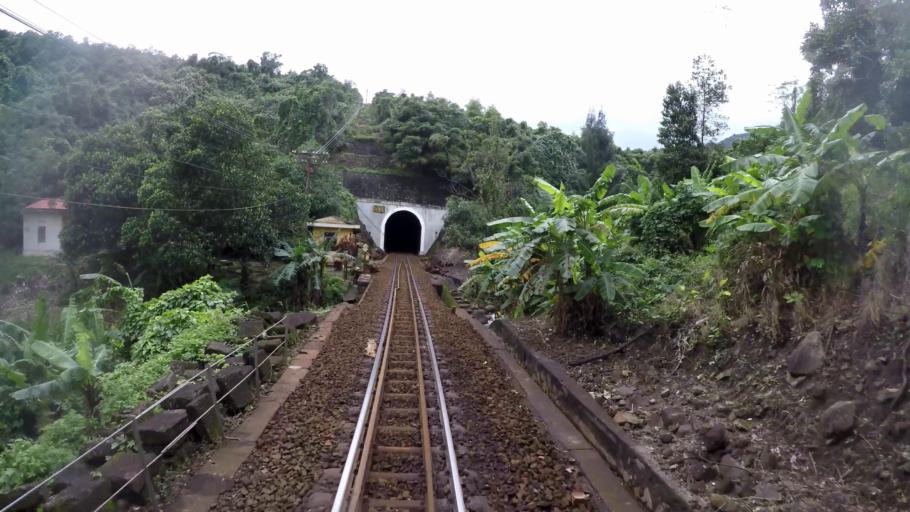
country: VN
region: Da Nang
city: Lien Chieu
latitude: 16.1722
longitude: 108.1440
